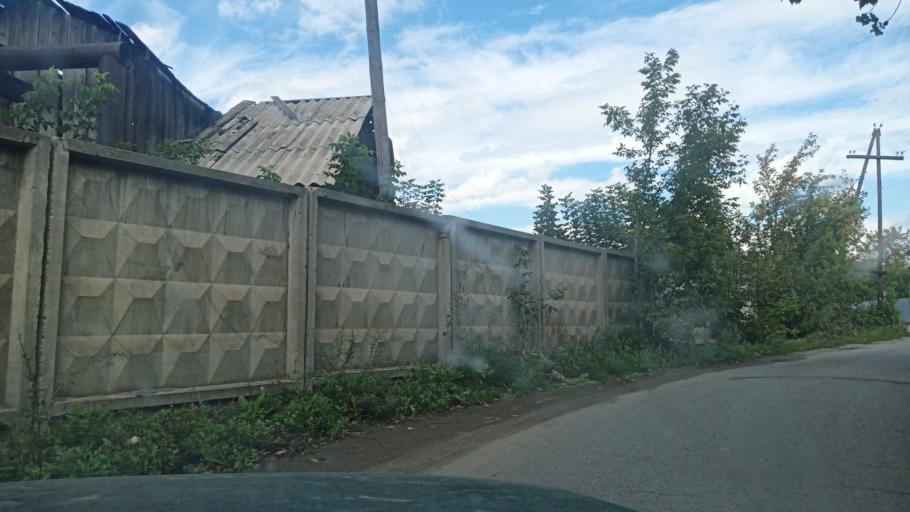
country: RU
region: Altai Krai
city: Zaton
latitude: 53.3325
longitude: 83.8062
